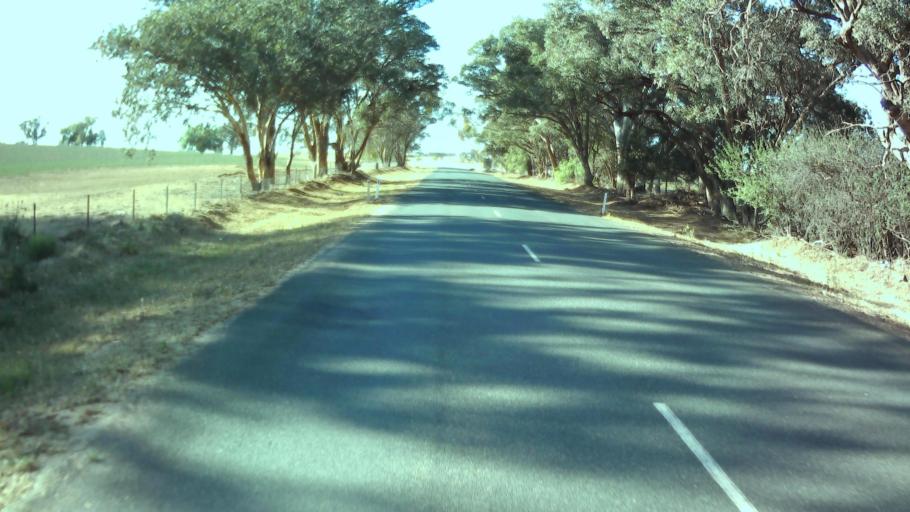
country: AU
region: New South Wales
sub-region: Weddin
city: Grenfell
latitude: -33.9823
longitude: 148.1404
